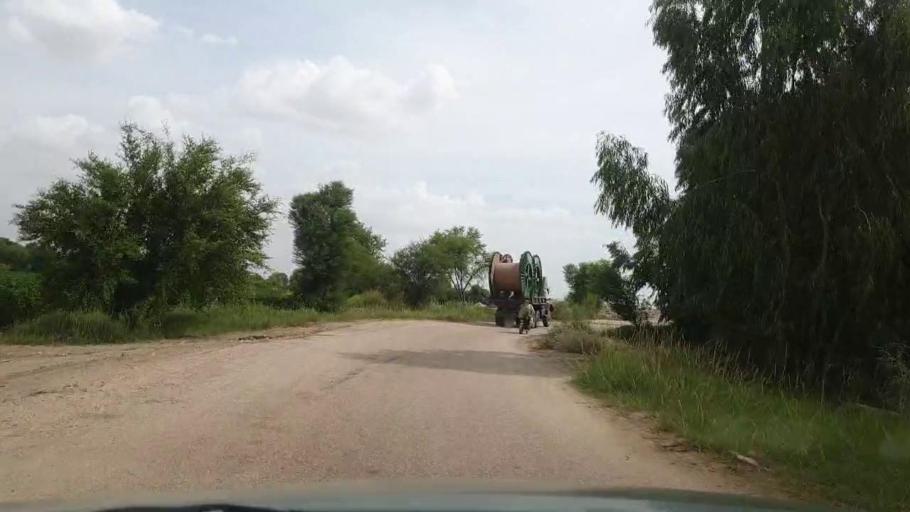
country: PK
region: Sindh
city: Kot Diji
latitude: 27.1553
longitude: 69.0352
